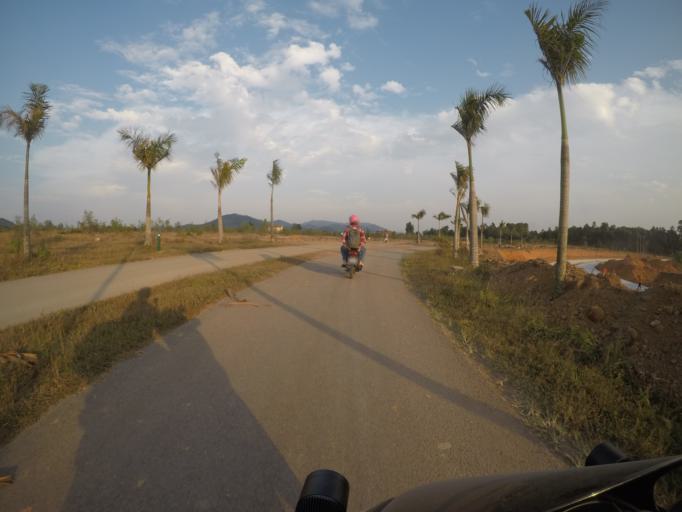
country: VN
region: Vinh Phuc
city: Phuc Yen
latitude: 21.3229
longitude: 105.7280
